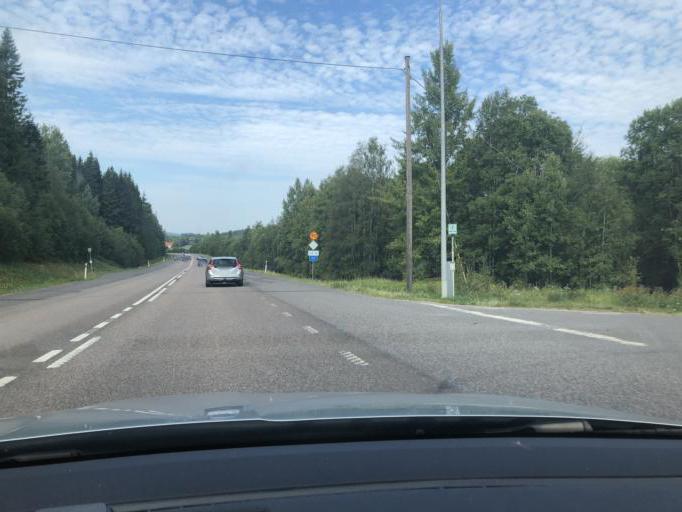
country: SE
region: Vaesternorrland
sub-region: Kramfors Kommun
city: Kramfors
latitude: 62.8966
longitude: 17.8483
